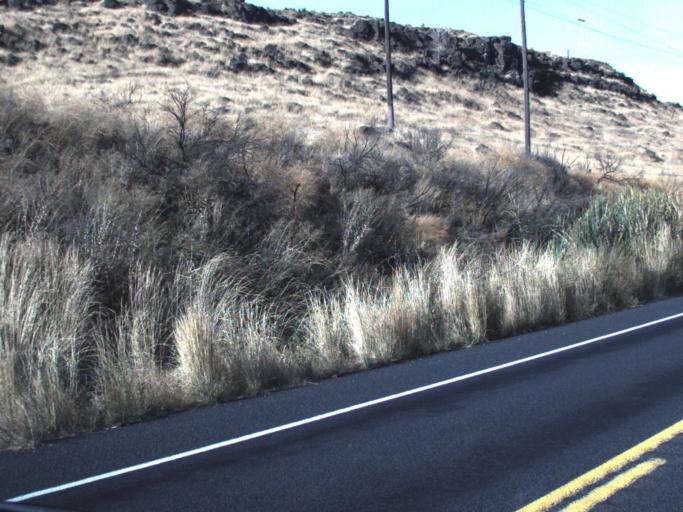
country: US
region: Oregon
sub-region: Morrow County
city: Boardman
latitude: 45.8998
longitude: -119.6845
